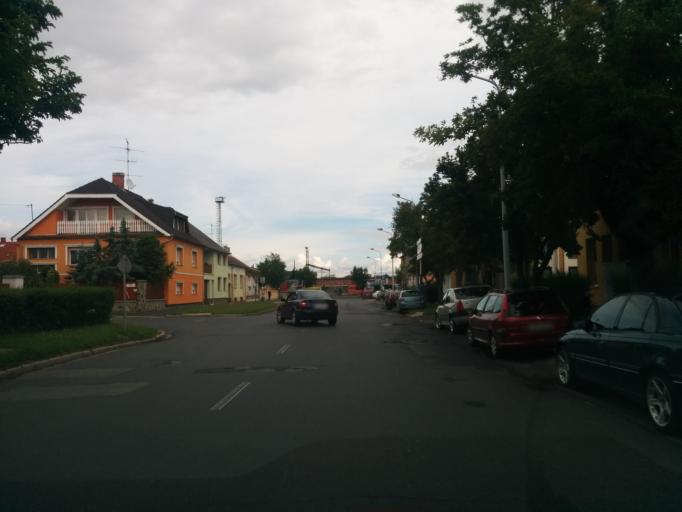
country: HU
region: Vas
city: Szombathely
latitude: 47.2391
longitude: 16.6296
